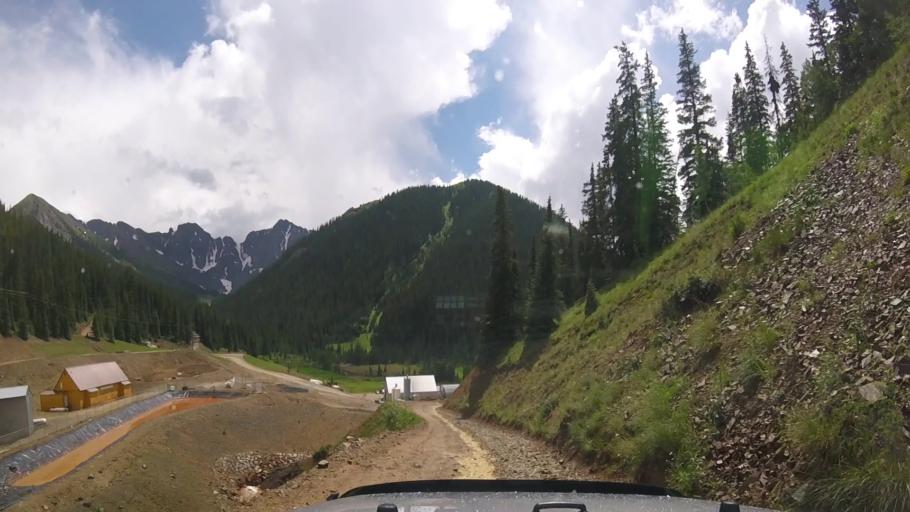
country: US
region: Colorado
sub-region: San Juan County
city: Silverton
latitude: 37.8917
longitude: -107.6495
